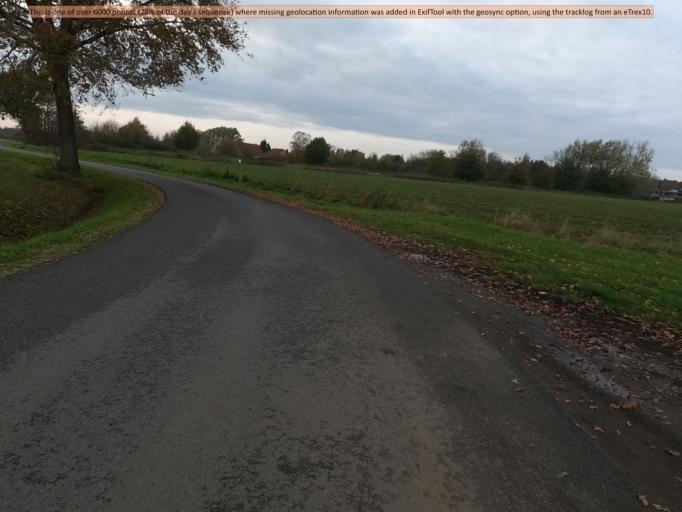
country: BE
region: Flanders
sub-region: Provincie Antwerpen
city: Lier
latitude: 51.1359
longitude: 4.6133
